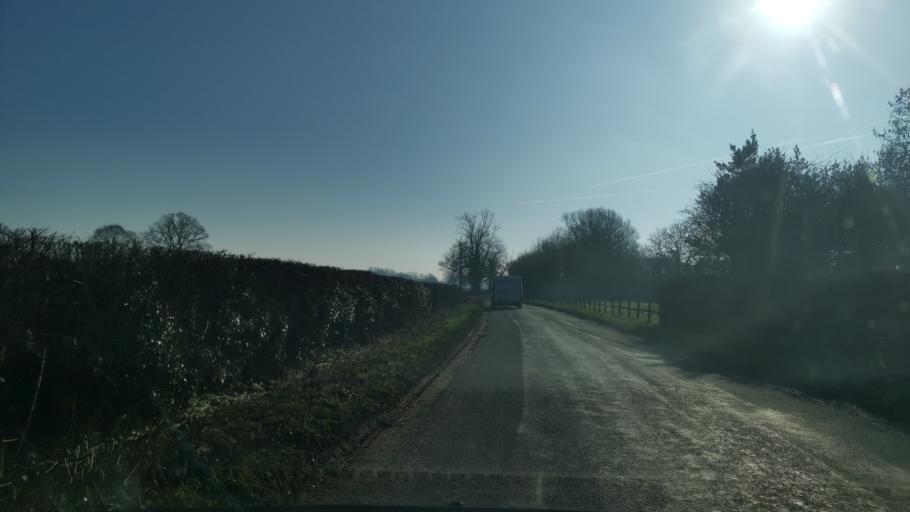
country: GB
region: England
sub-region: City of York
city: Murton
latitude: 53.9700
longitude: -1.0096
